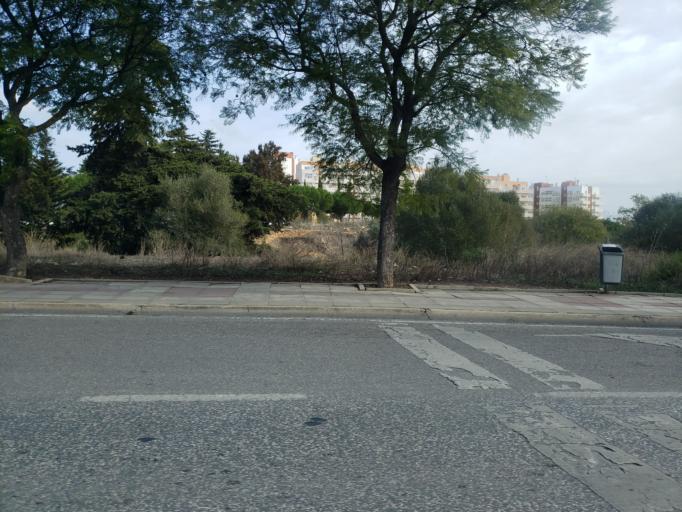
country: PT
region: Faro
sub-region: Portimao
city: Portimao
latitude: 37.1431
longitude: -8.5482
